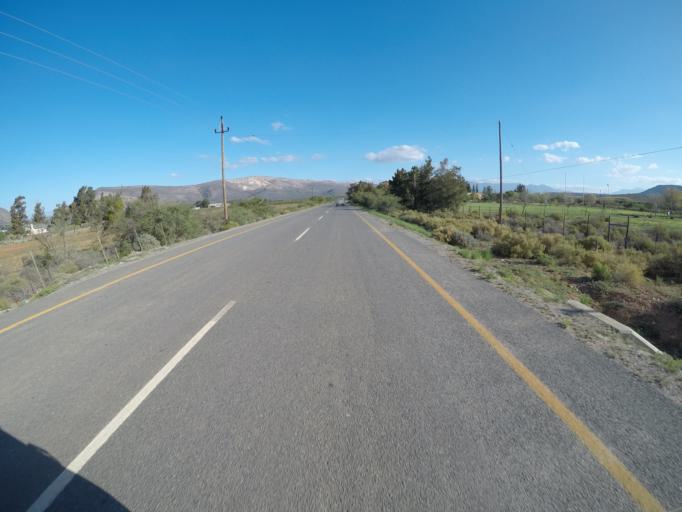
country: ZA
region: Western Cape
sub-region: Cape Winelands District Municipality
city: Ashton
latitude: -33.8078
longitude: 19.7823
